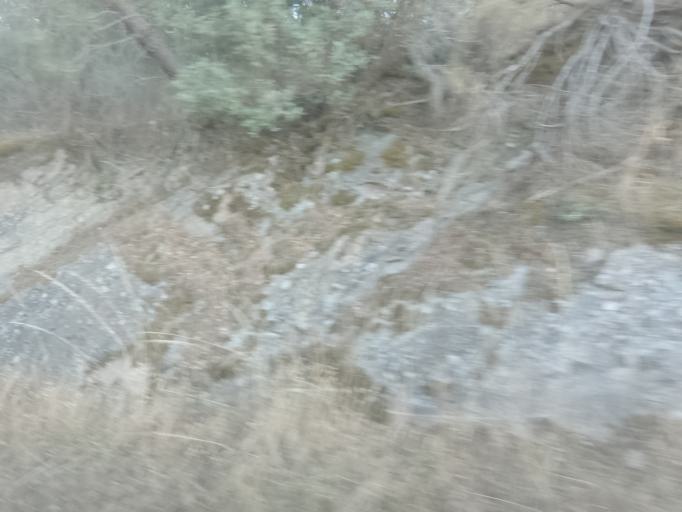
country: PT
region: Viseu
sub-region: Tabuaco
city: Tabuaco
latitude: 41.1484
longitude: -7.6065
